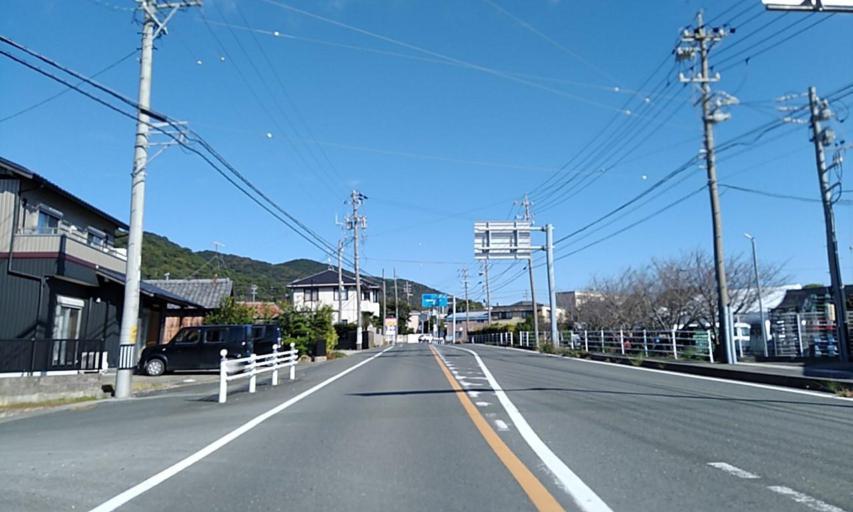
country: JP
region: Aichi
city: Tahara
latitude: 34.6540
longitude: 137.2433
